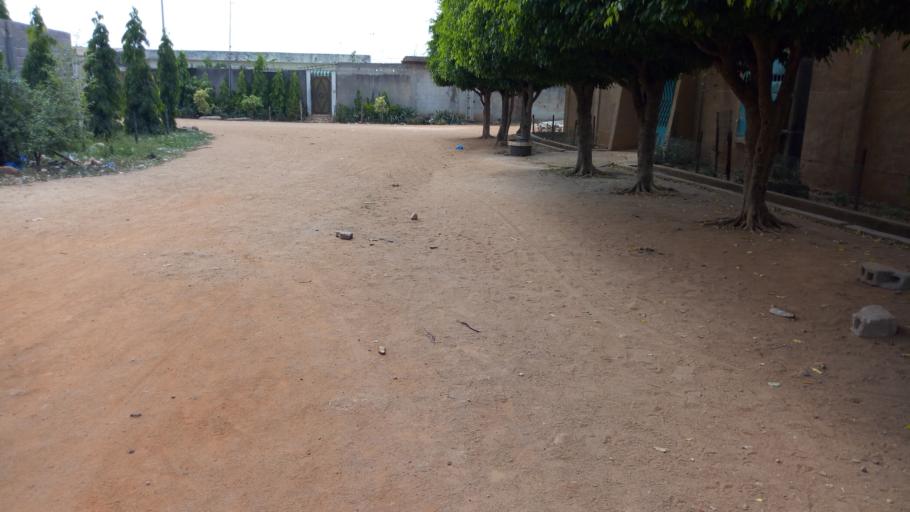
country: CI
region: Vallee du Bandama
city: Bouake
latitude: 7.7057
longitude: -5.0467
